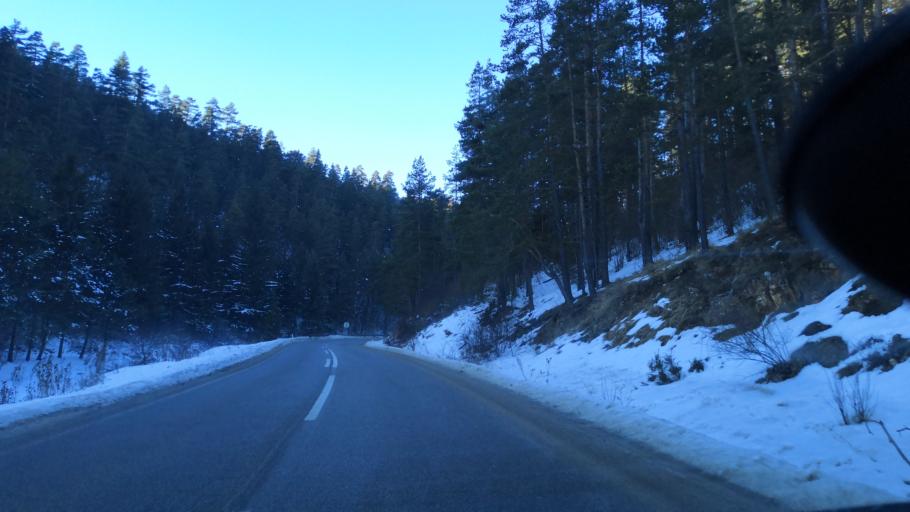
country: BA
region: Republika Srpska
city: Sokolac
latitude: 43.9712
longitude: 18.8571
